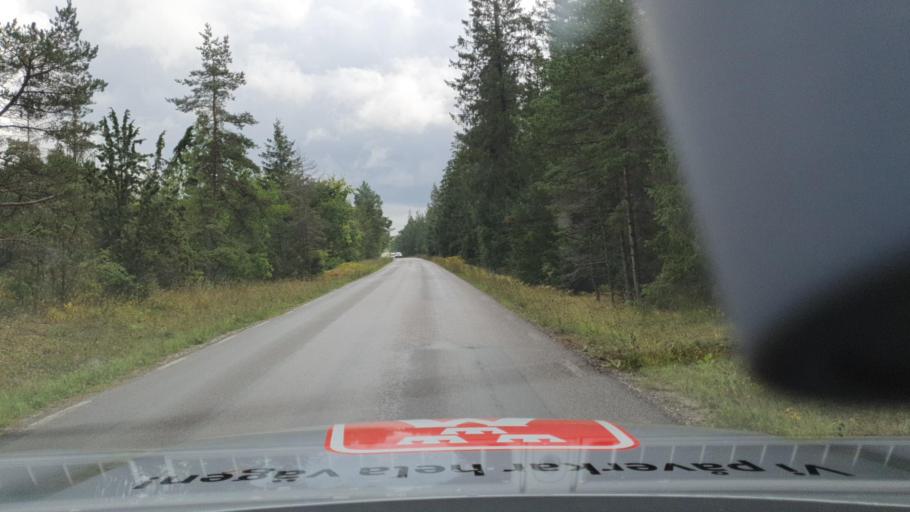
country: SE
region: Gotland
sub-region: Gotland
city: Slite
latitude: 57.7160
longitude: 18.7527
